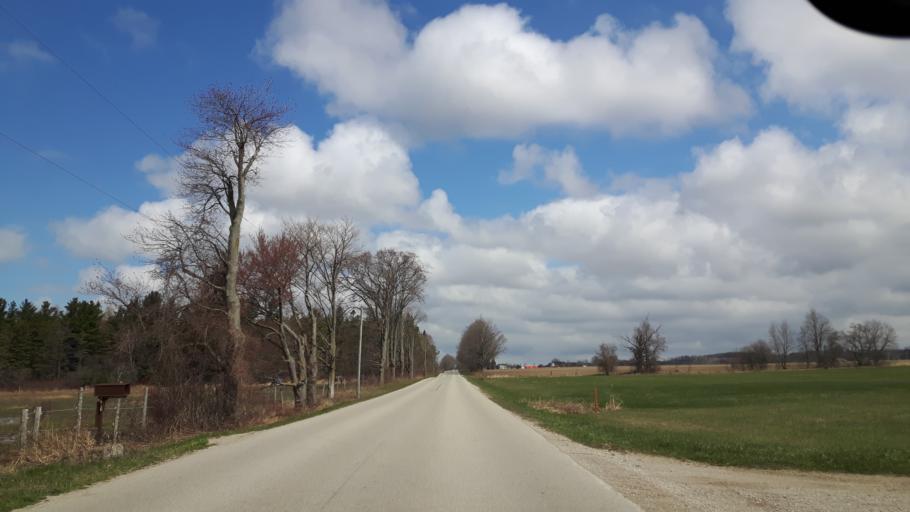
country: CA
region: Ontario
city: Goderich
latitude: 43.6300
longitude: -81.6846
